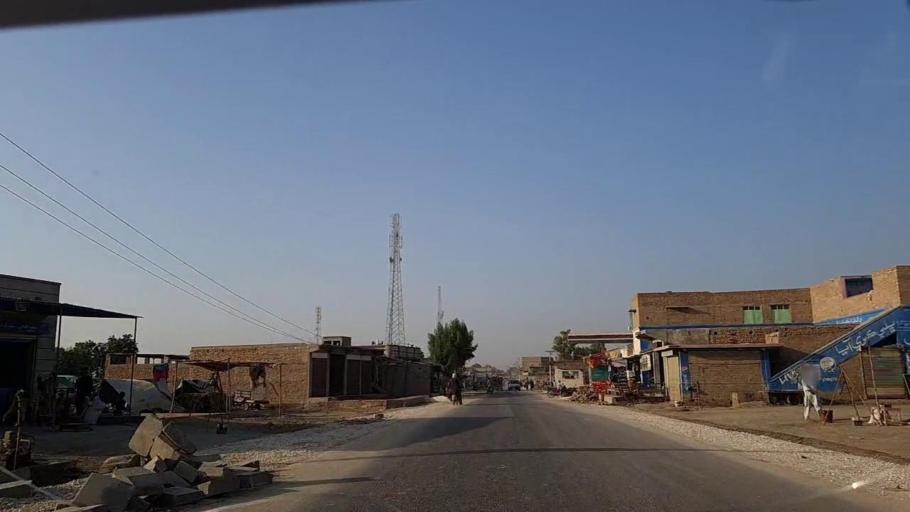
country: PK
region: Sindh
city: Rustam jo Goth
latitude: 27.9619
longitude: 68.8061
